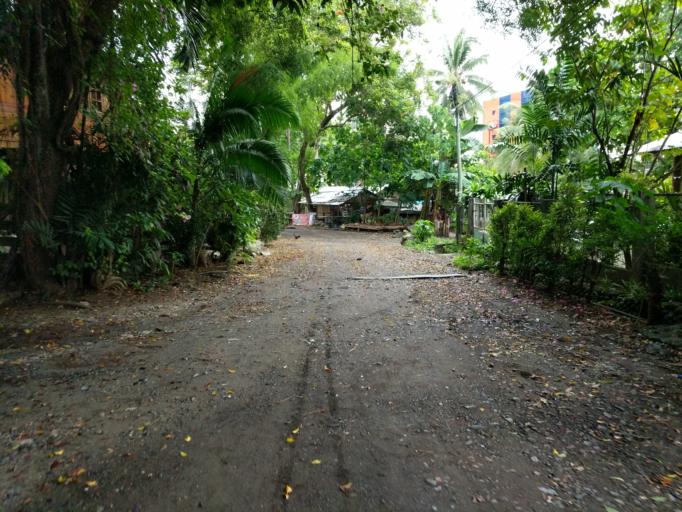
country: PH
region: Davao
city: Davao
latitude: 7.0786
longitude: 125.5819
